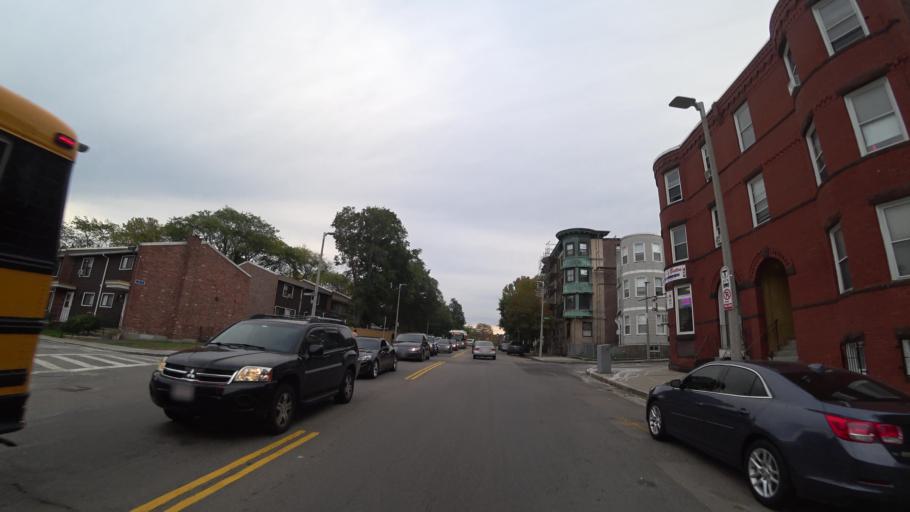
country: US
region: Massachusetts
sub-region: Suffolk County
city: Jamaica Plain
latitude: 42.3185
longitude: -71.0862
